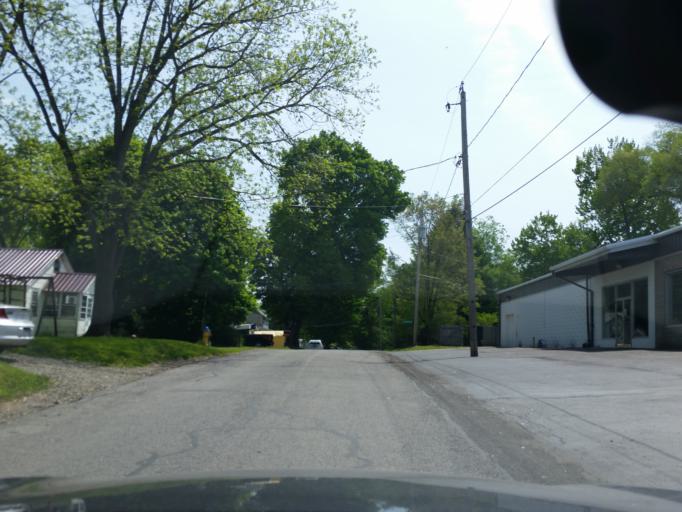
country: US
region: New York
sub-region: Chautauqua County
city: Celoron
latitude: 42.0995
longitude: -79.2988
